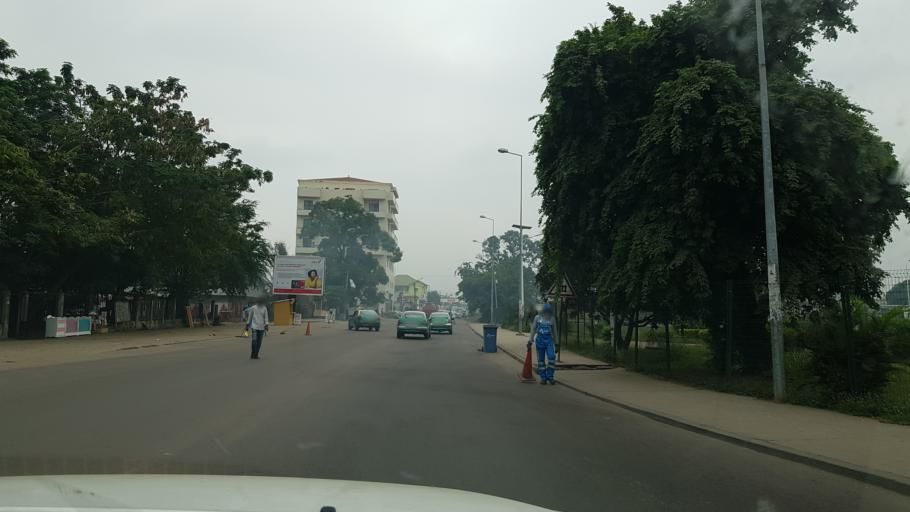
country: CG
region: Brazzaville
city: Brazzaville
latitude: -4.2637
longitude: 15.2608
